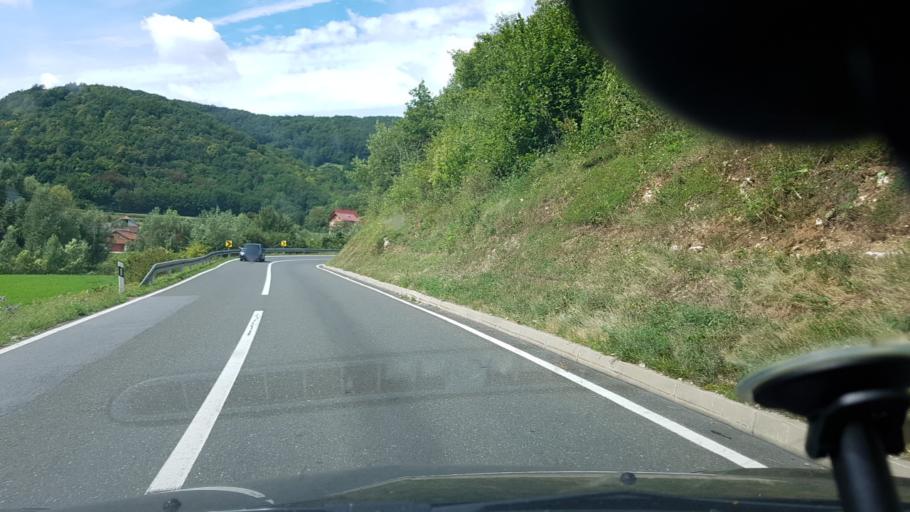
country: HR
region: Varazdinska
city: Lepoglava
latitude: 46.2141
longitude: 15.9972
